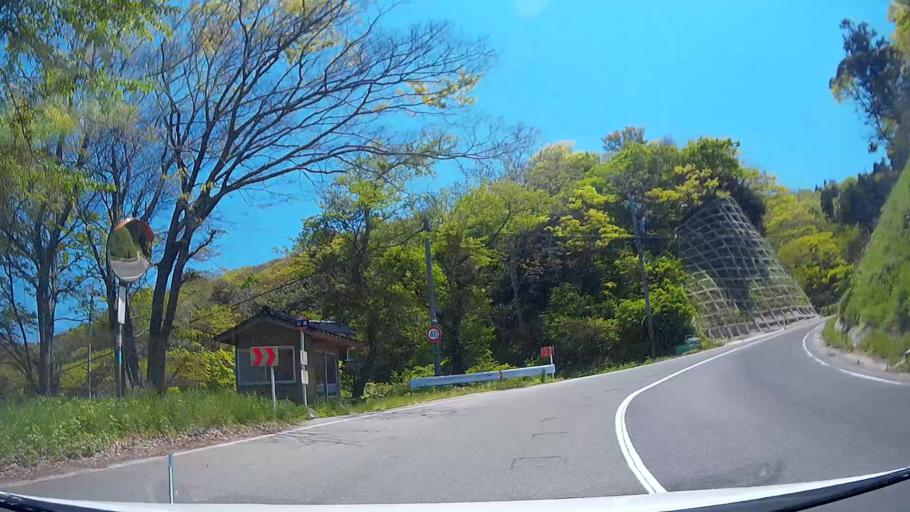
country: JP
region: Ishikawa
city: Nanao
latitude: 37.5250
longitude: 137.2996
